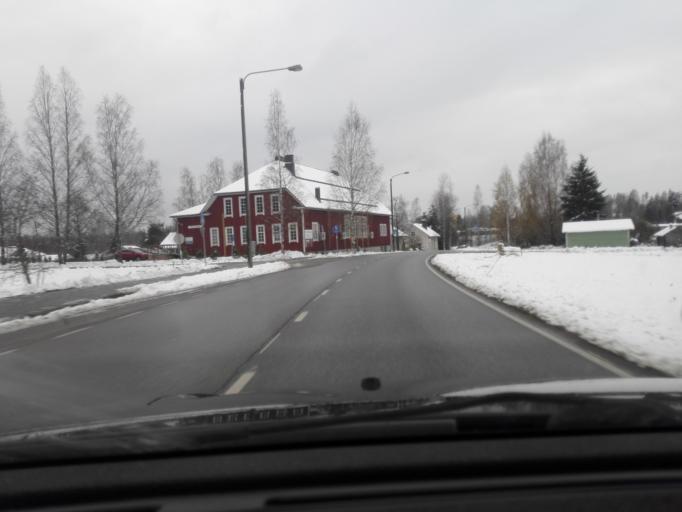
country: FI
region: Uusimaa
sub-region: Helsinki
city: Vihti
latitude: 60.4176
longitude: 24.3448
